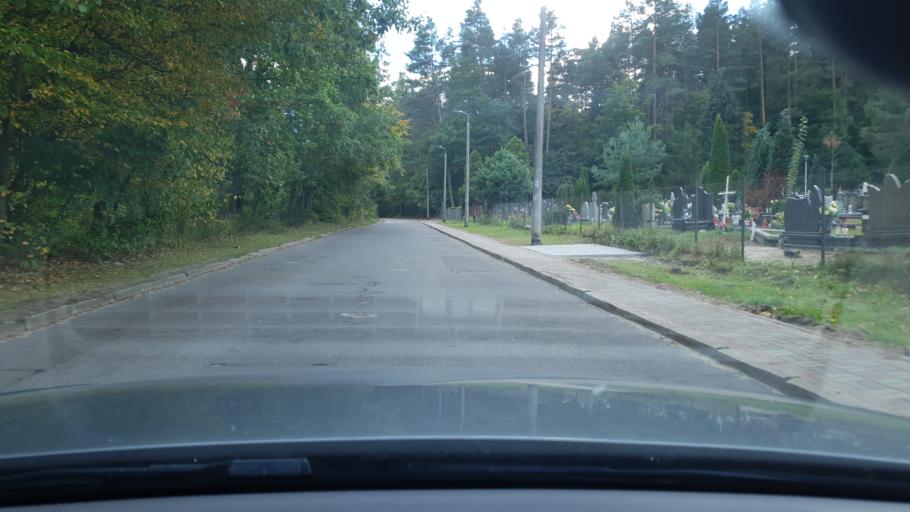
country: PL
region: Pomeranian Voivodeship
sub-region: Powiat wejherowski
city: Reda
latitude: 54.5921
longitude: 18.3364
